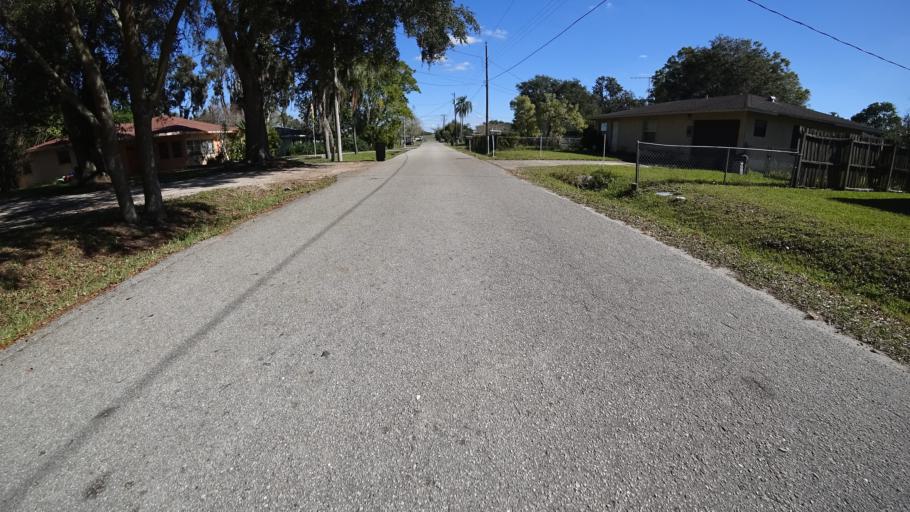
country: US
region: Florida
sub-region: Manatee County
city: West Samoset
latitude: 27.4788
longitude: -82.5567
